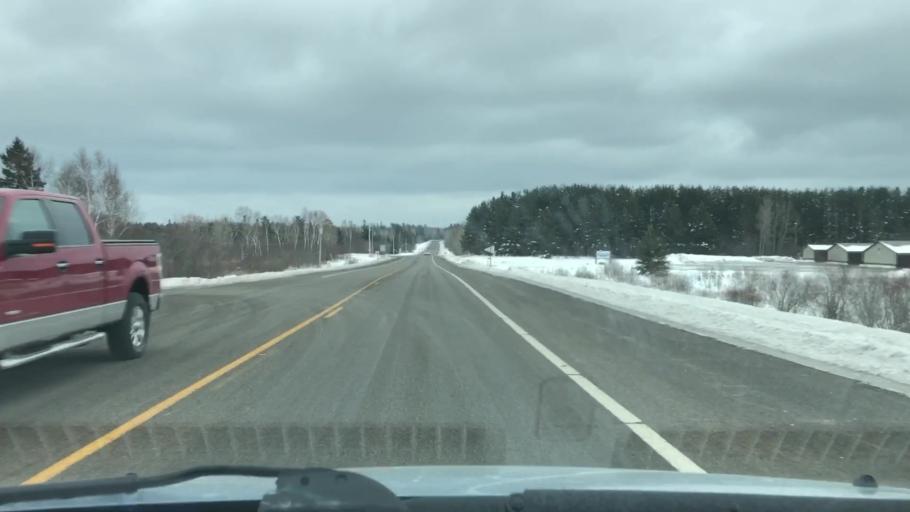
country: US
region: Minnesota
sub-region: Carlton County
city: Esko
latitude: 46.6945
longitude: -92.3650
